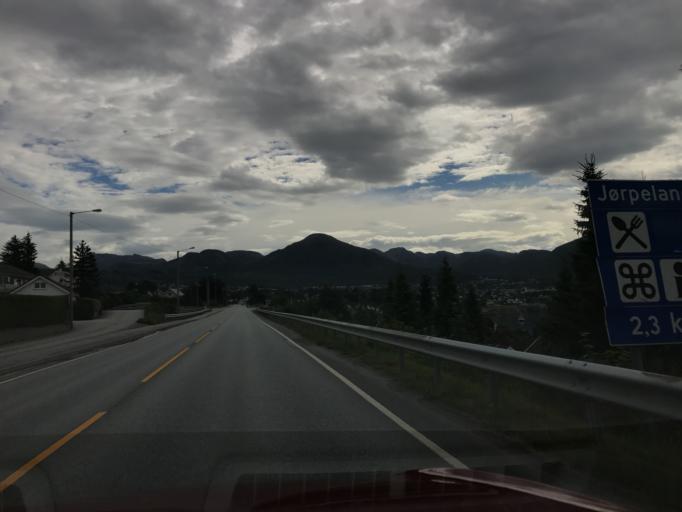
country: NO
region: Rogaland
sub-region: Strand
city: Jorpeland
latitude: 59.0230
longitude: 6.0060
